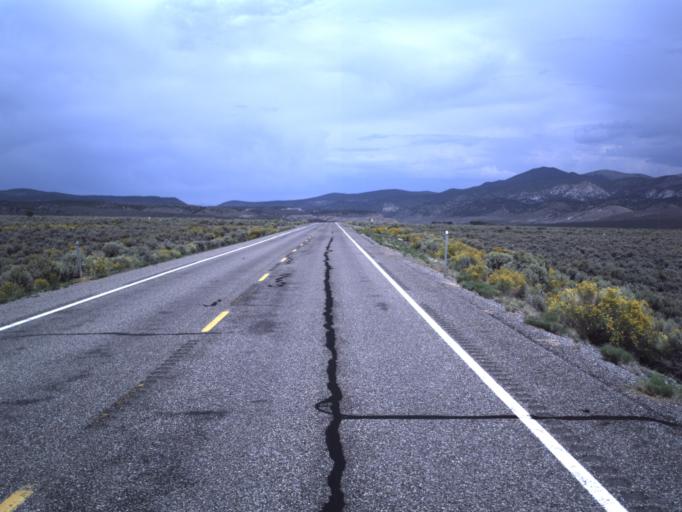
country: US
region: Utah
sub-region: Garfield County
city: Panguitch
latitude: 37.9862
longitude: -112.3964
